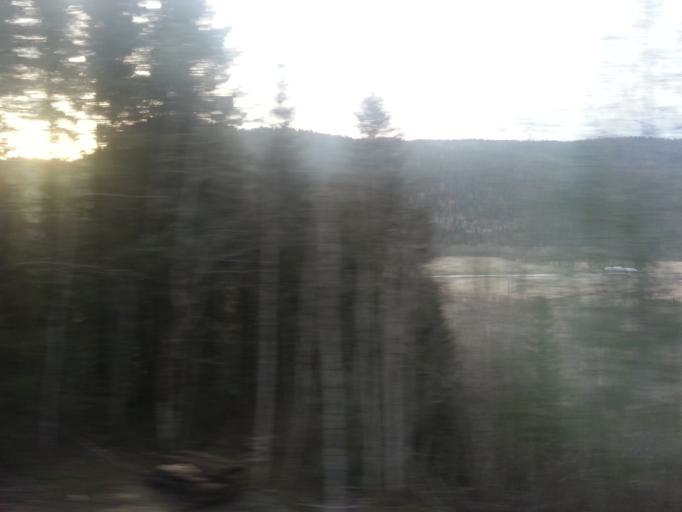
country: NO
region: Sor-Trondelag
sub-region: Midtre Gauldal
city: Storen
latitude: 63.0164
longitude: 10.2386
